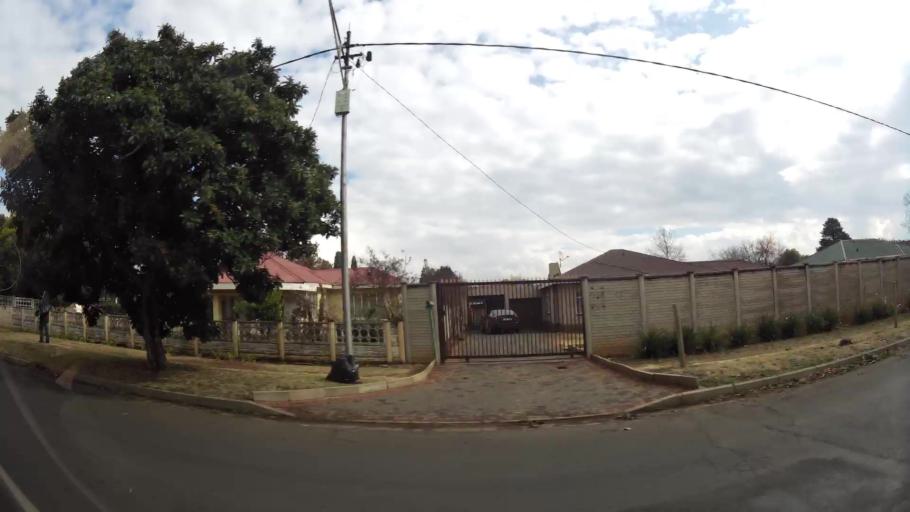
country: ZA
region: Gauteng
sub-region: Sedibeng District Municipality
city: Vereeniging
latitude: -26.6492
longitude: 27.9691
